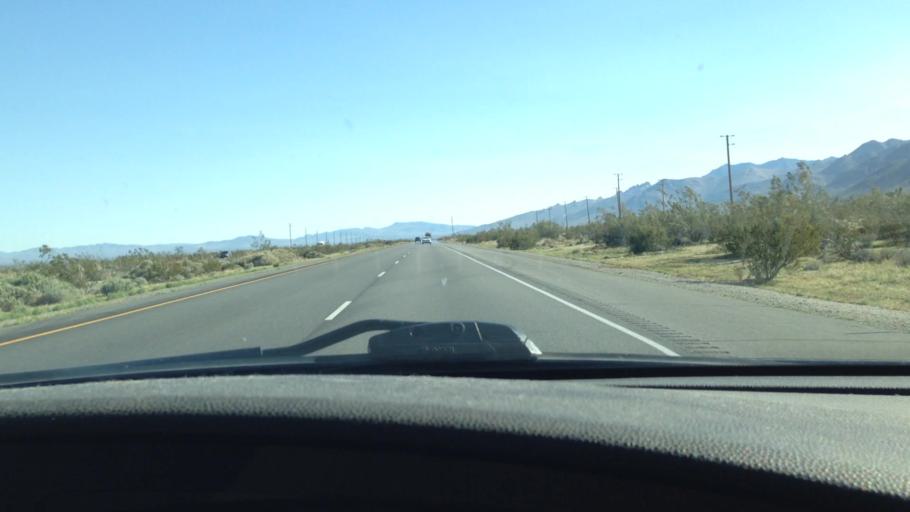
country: US
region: California
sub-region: Kern County
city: Inyokern
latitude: 35.8407
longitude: -117.8751
